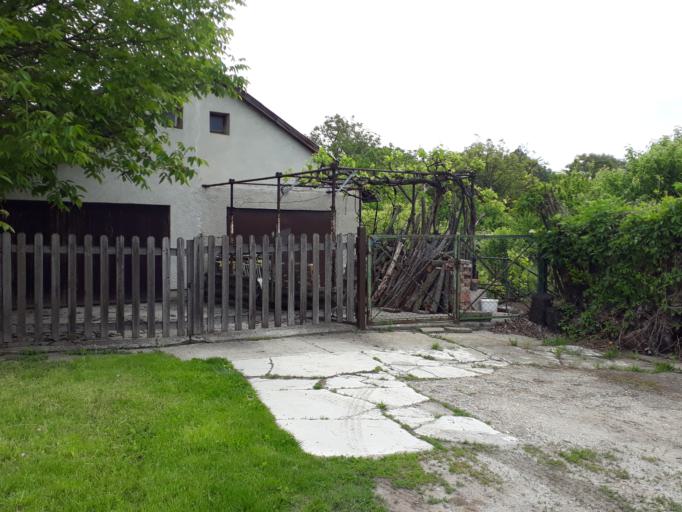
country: HU
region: Budapest
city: Budapest XII. keruelet
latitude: 47.4603
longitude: 19.0074
